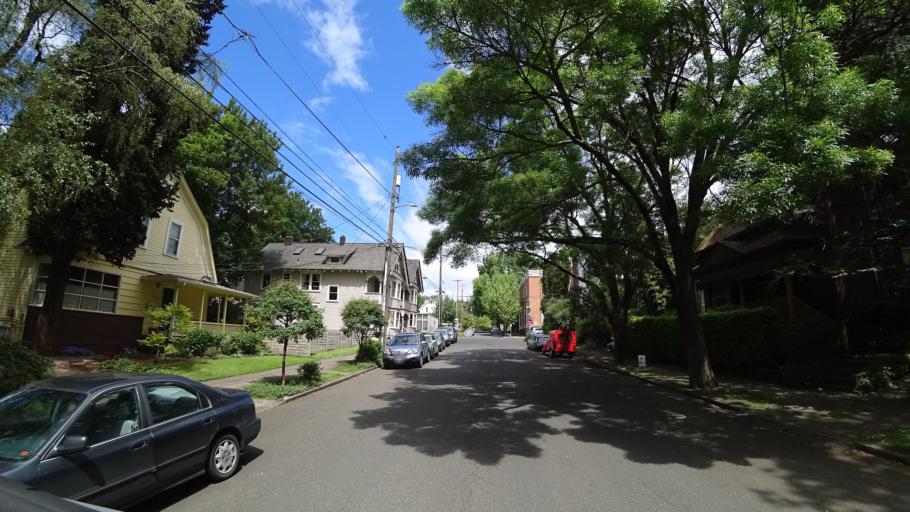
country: US
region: Oregon
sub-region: Multnomah County
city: Portland
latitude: 45.5159
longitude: -122.6486
